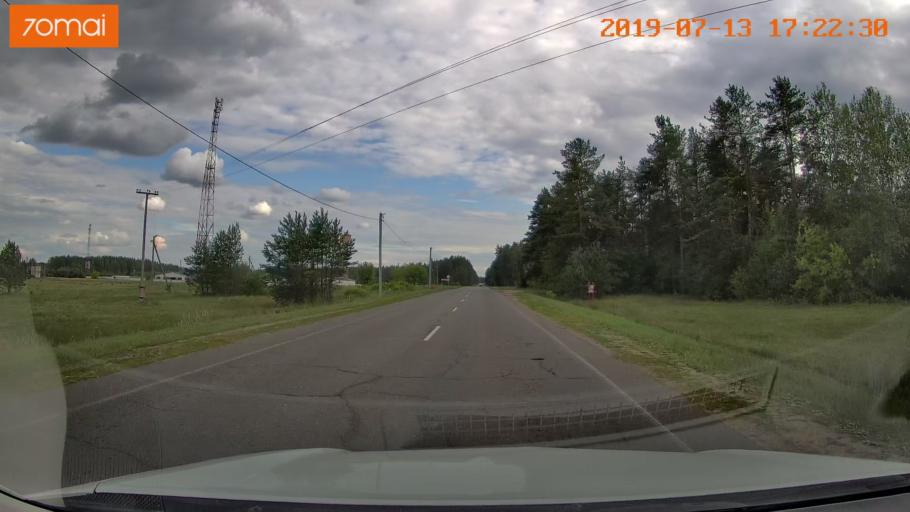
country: BY
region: Mogilev
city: Babruysk
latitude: 53.2705
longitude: 29.2345
